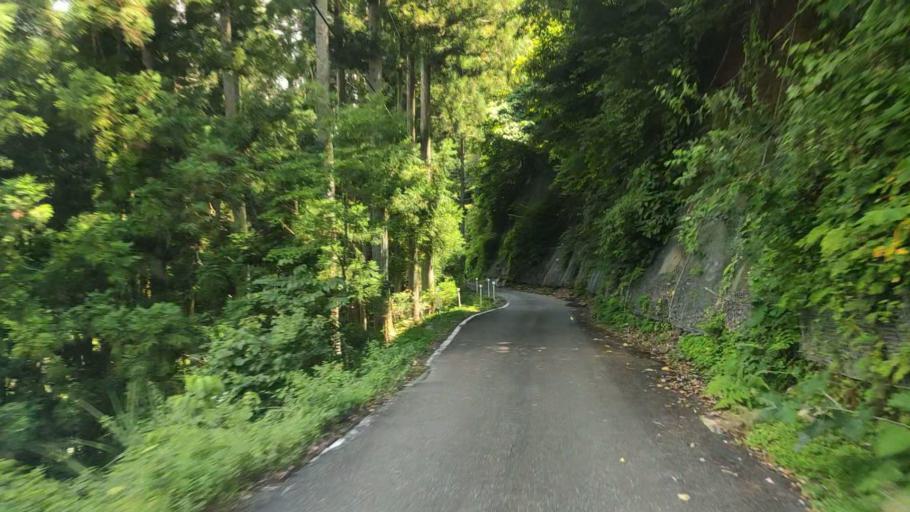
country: JP
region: Fukui
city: Ono
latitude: 35.7203
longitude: 136.5829
